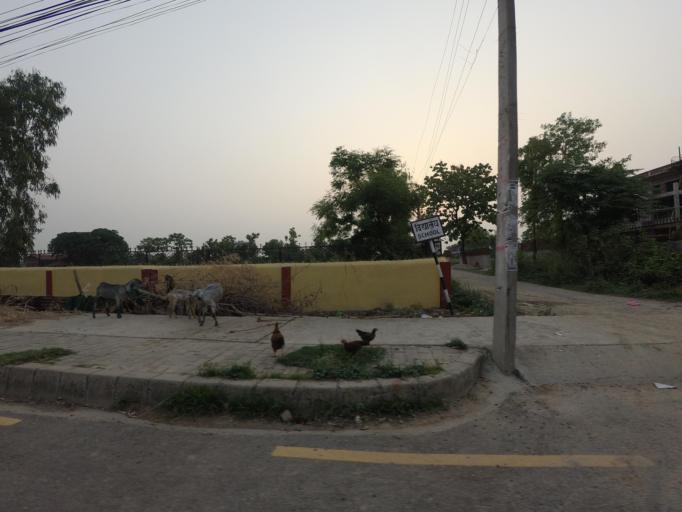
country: NP
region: Western Region
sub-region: Lumbini Zone
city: Bhairahawa
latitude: 27.5014
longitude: 83.4633
